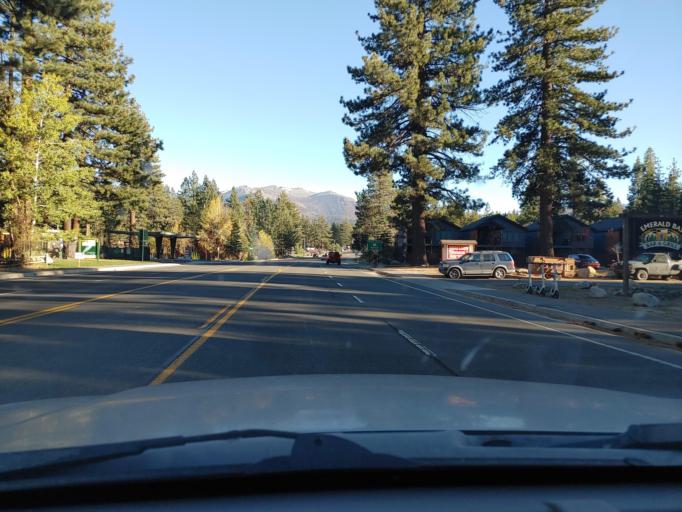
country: US
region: California
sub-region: El Dorado County
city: South Lake Tahoe
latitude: 38.9162
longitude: -120.0080
